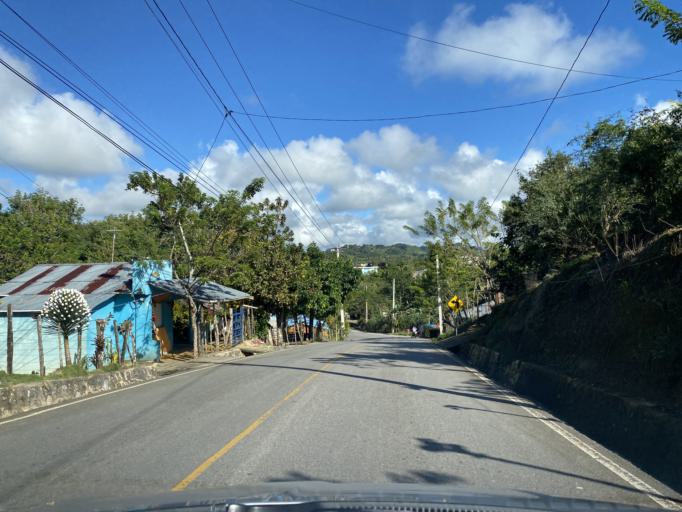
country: DO
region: Samana
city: Sanchez
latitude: 19.2510
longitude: -69.5848
